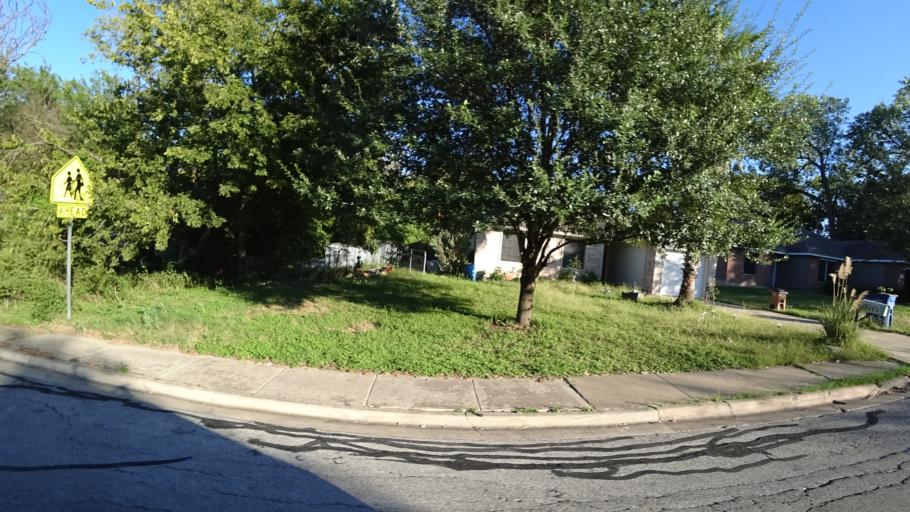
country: US
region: Texas
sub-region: Travis County
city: Austin
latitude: 30.2224
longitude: -97.7366
